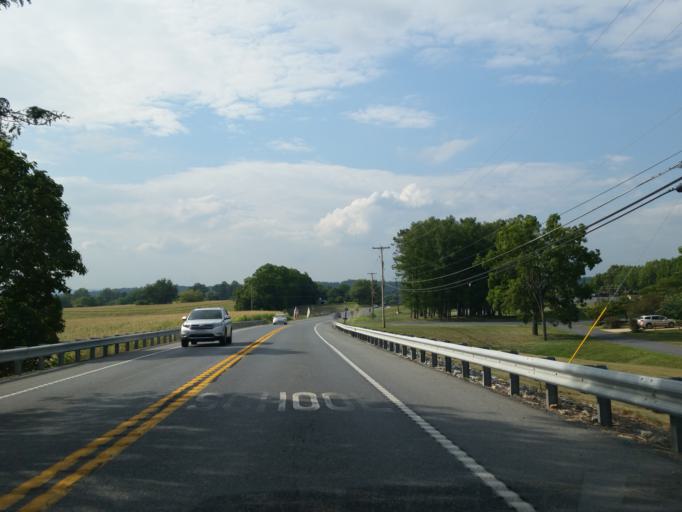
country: US
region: Pennsylvania
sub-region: Lebanon County
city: Annville
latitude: 40.3170
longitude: -76.5072
